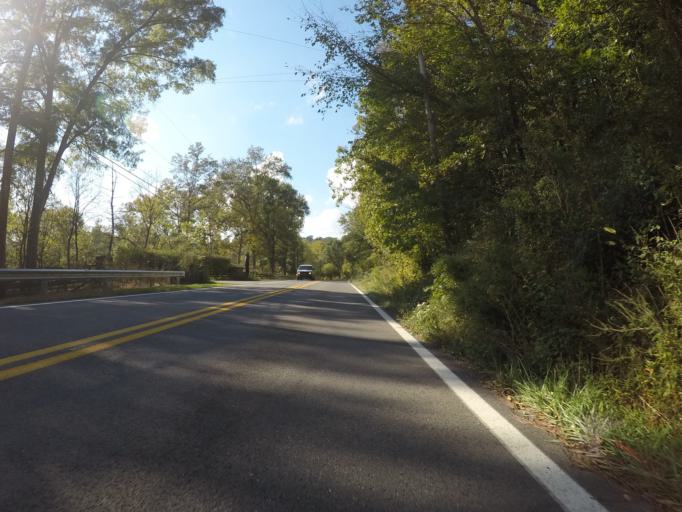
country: US
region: Ohio
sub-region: Lawrence County
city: Burlington
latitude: 38.3735
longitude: -82.5293
